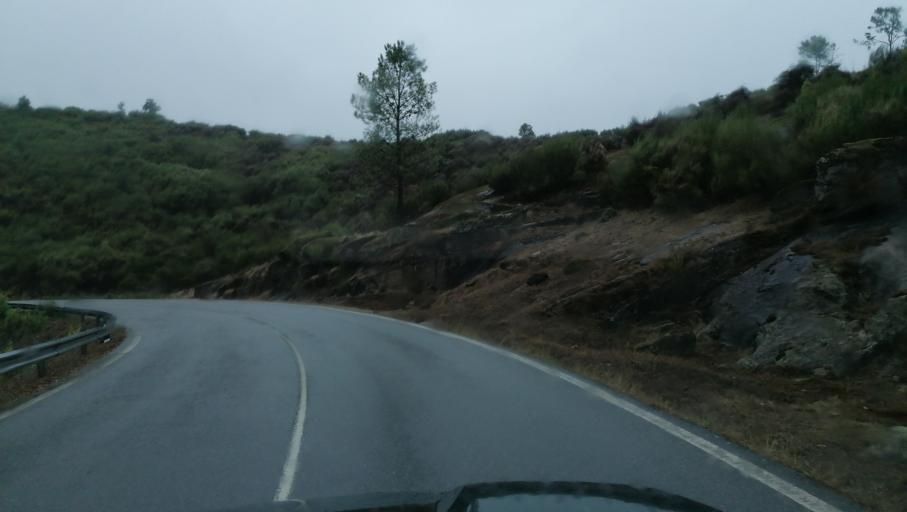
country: PT
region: Braga
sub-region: Cabeceiras de Basto
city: Cabeceiras de Basto
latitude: 41.4904
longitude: -7.9338
